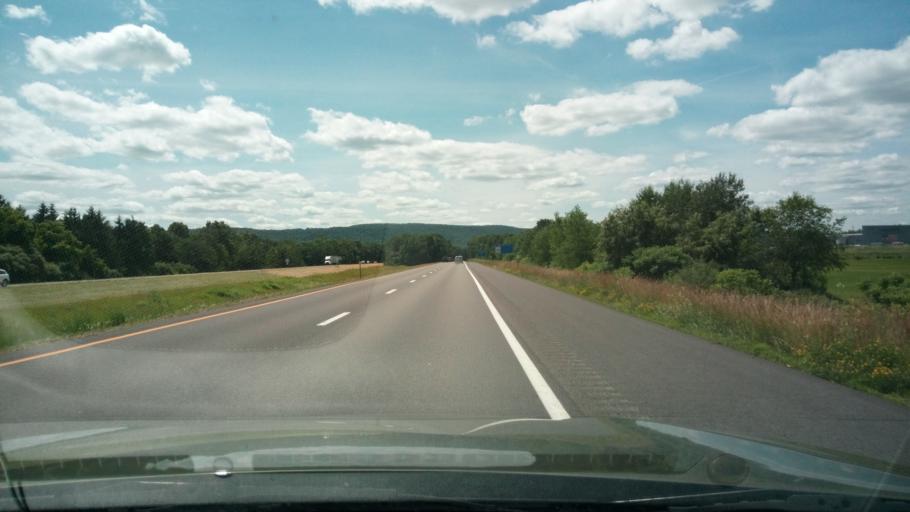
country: US
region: Pennsylvania
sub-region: Bradford County
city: South Waverly
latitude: 42.0013
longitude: -76.6083
